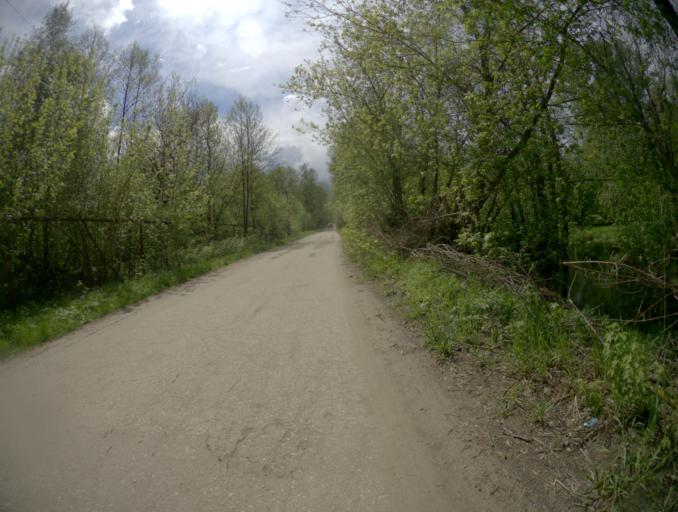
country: RU
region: Vladimir
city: Velikodvorskiy
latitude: 55.2424
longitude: 40.6712
